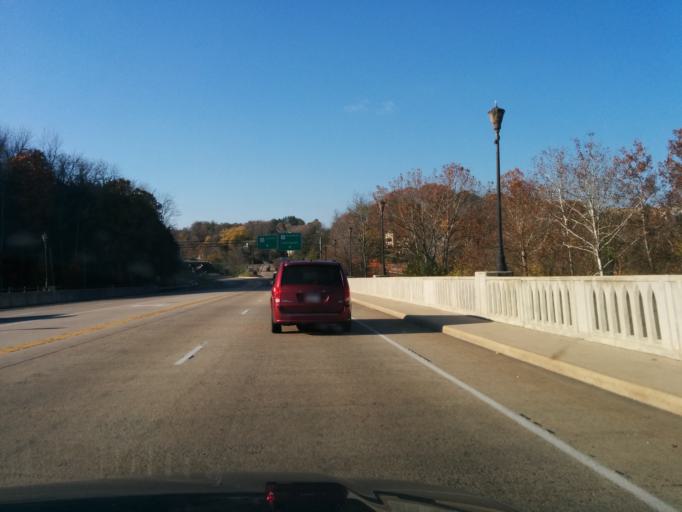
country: US
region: Virginia
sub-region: Rockbridge County
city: East Lexington
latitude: 37.7923
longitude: -79.4270
